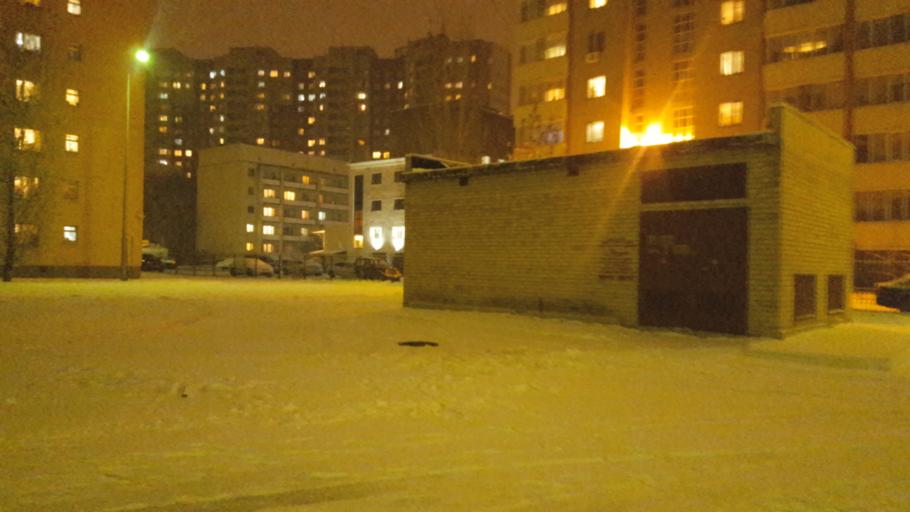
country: KZ
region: Astana Qalasy
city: Astana
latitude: 51.1525
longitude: 71.4833
